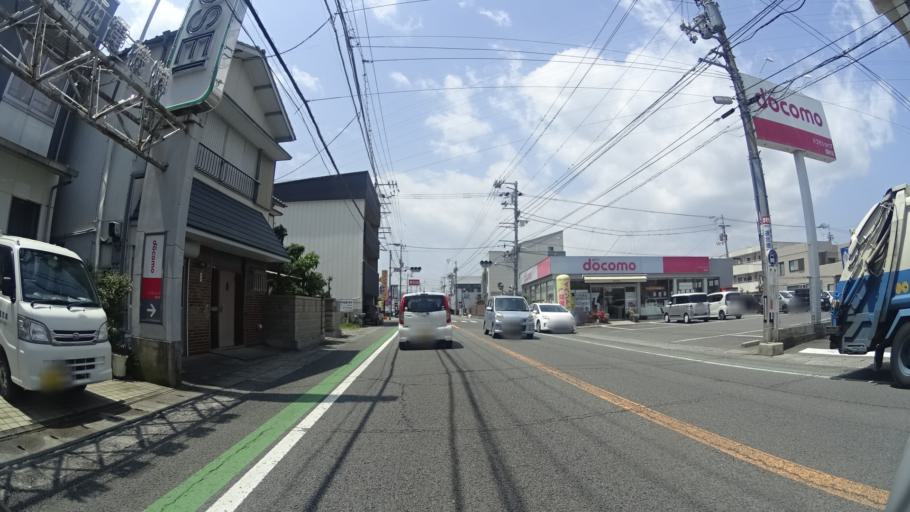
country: JP
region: Tokushima
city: Ishii
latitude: 34.0724
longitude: 134.4883
